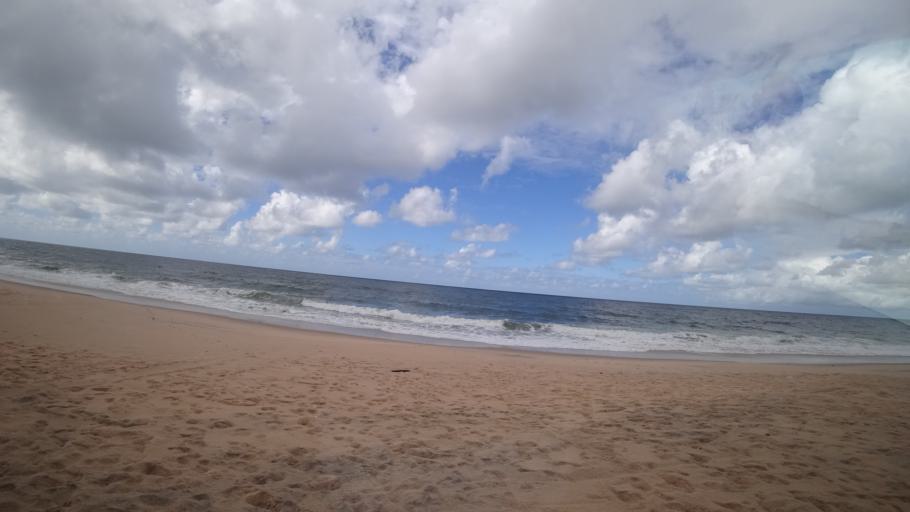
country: MZ
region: Sofala
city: Beira
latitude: -19.6163
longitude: 35.2197
